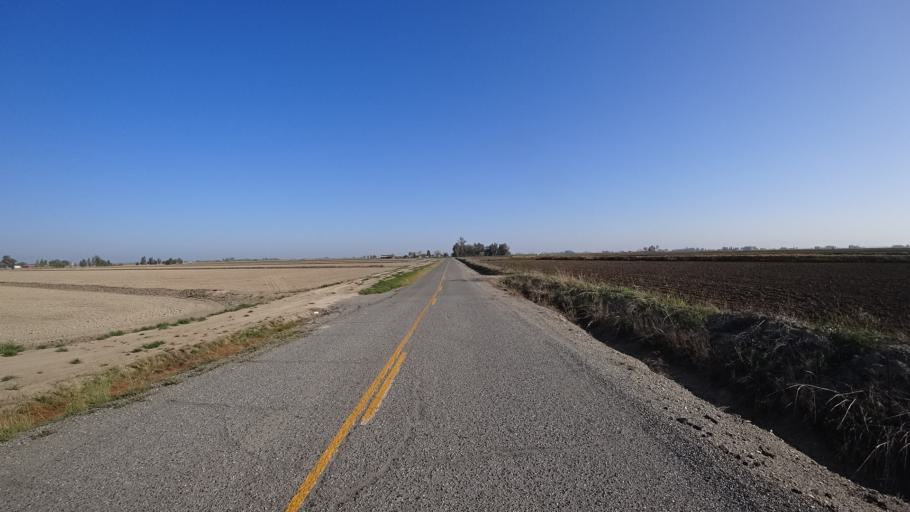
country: US
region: California
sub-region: Glenn County
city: Willows
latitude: 39.5240
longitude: -122.1217
